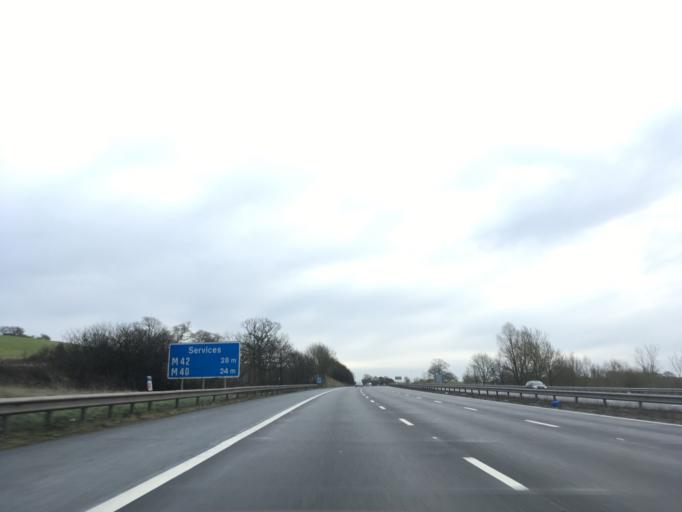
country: GB
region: England
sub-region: Worcestershire
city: Alvechurch
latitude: 52.3593
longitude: -1.9323
